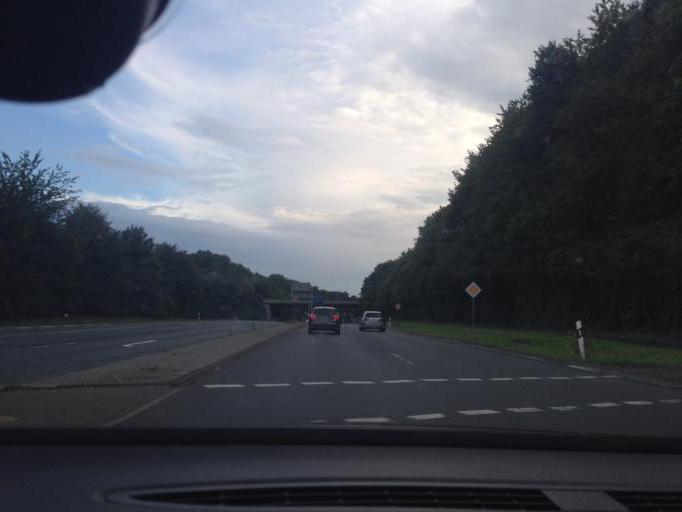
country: DE
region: Hesse
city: Lollar
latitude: 50.6259
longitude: 8.7071
